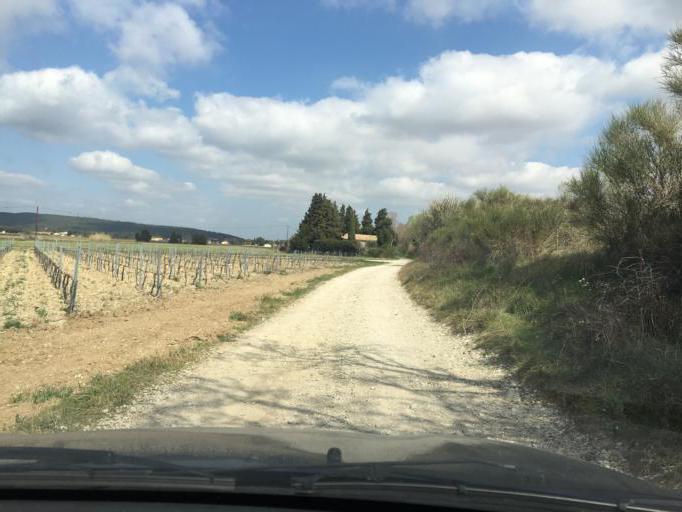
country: FR
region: Provence-Alpes-Cote d'Azur
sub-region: Departement du Vaucluse
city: Serignan-du-Comtat
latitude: 44.1717
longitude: 4.8291
